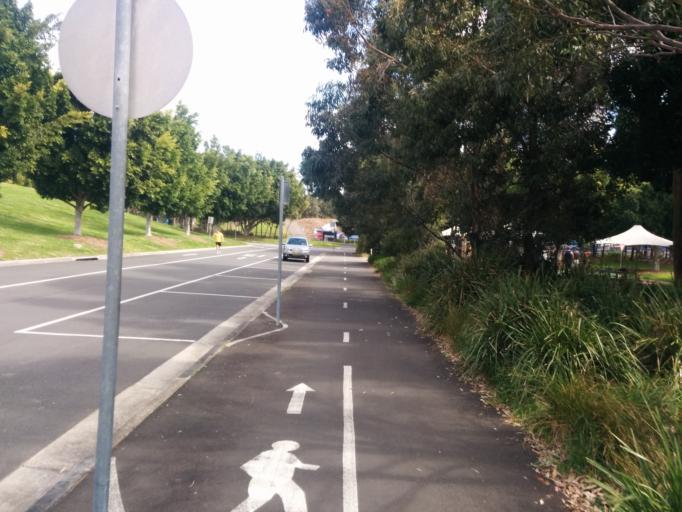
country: AU
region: New South Wales
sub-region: Canada Bay
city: Concord West
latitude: -33.8473
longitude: 151.0764
